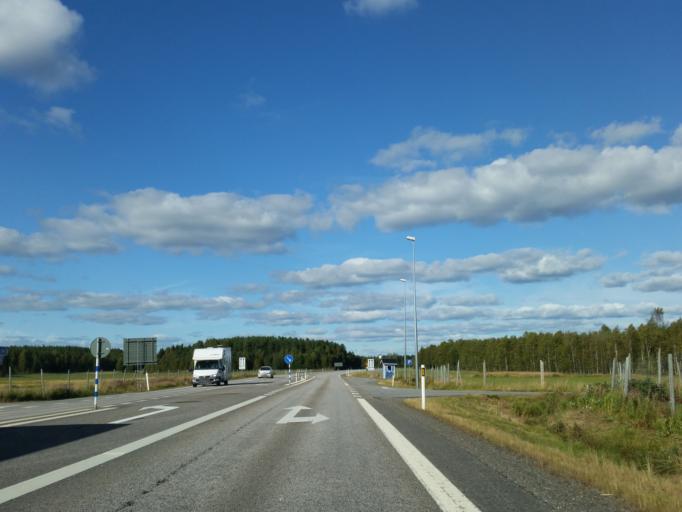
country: SE
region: Vaesterbotten
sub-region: Robertsfors Kommun
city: Robertsfors
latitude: 64.1385
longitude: 20.8943
